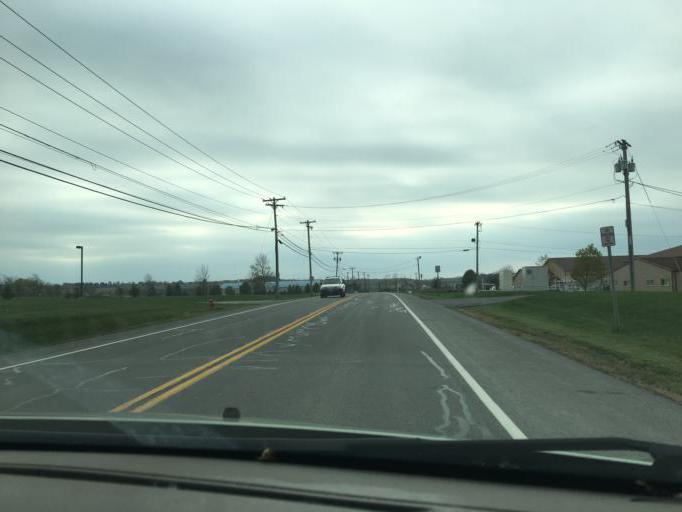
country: US
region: New York
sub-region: Ontario County
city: Canandaigua
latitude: 42.9008
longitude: -77.3041
